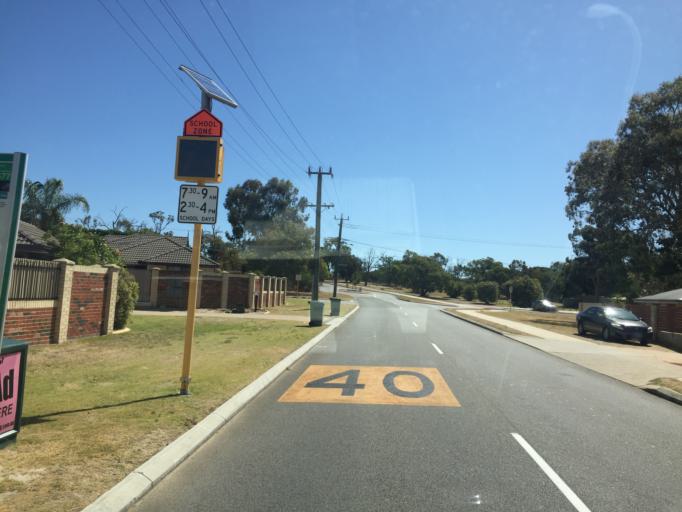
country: AU
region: Western Australia
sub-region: Belmont
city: Redcliffe
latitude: -31.9354
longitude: 115.9471
